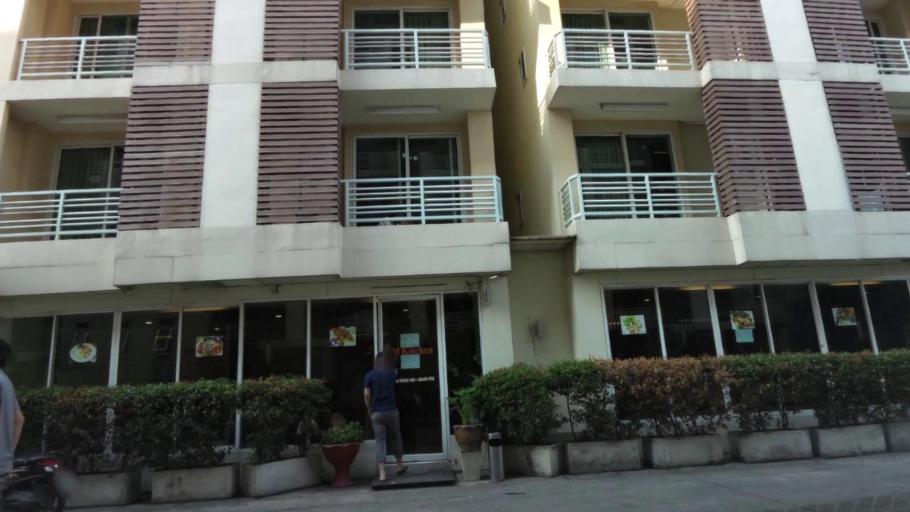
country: TH
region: Phra Nakhon Si Ayutthaya
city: Uthai
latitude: 14.3205
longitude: 100.6305
